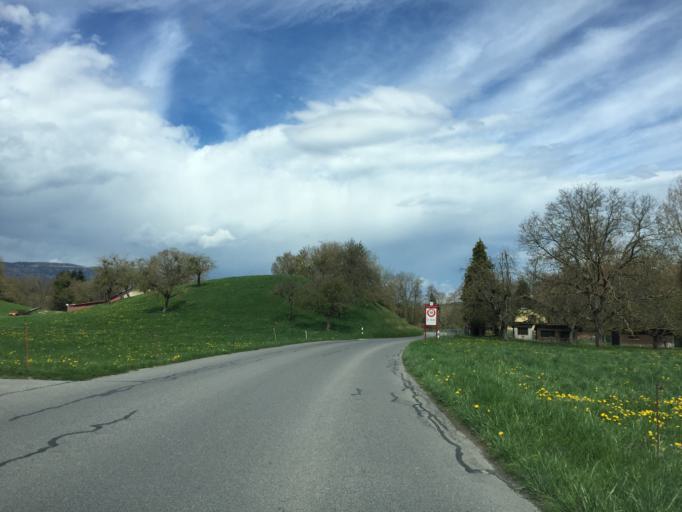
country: CH
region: Vaud
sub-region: Morges District
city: Chavannes-le-Veyron
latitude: 46.6041
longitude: 6.4592
